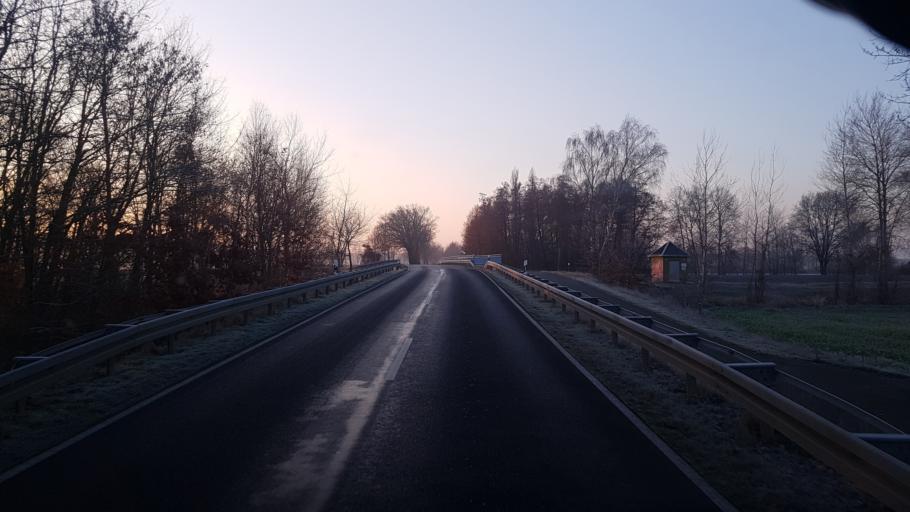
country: DE
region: Brandenburg
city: Tettau
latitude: 51.4607
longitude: 13.7396
